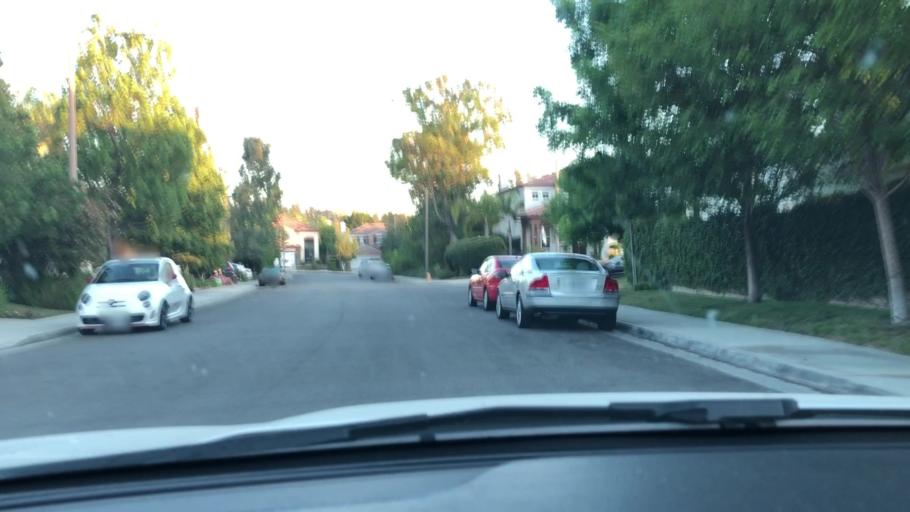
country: US
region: California
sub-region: Los Angeles County
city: Santa Clarita
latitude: 34.4577
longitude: -118.5440
